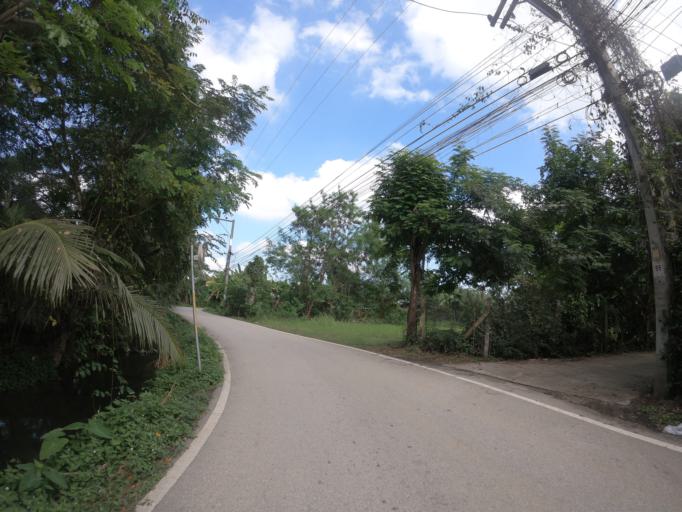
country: TH
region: Chiang Mai
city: Saraphi
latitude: 18.7181
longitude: 99.0153
